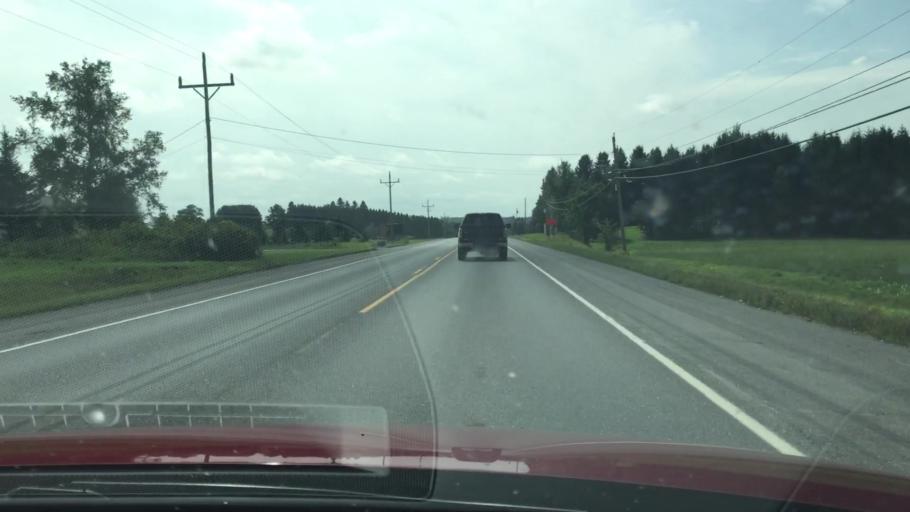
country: US
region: Maine
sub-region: Aroostook County
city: Easton
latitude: 46.4922
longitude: -67.8685
